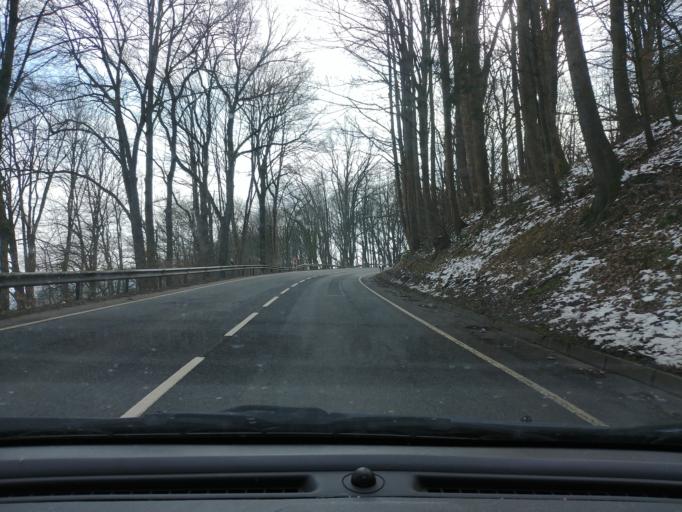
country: DE
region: Lower Saxony
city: Bodenfelde
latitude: 51.6865
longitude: 9.5169
